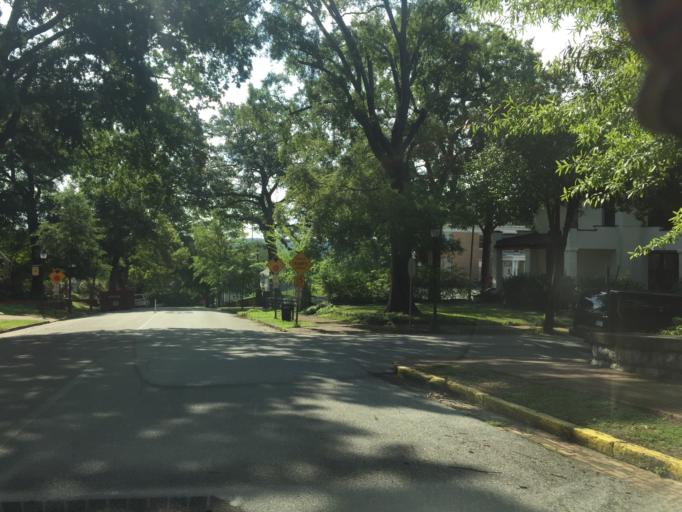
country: US
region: Tennessee
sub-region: Hamilton County
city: Chattanooga
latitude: 35.0445
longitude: -85.2913
